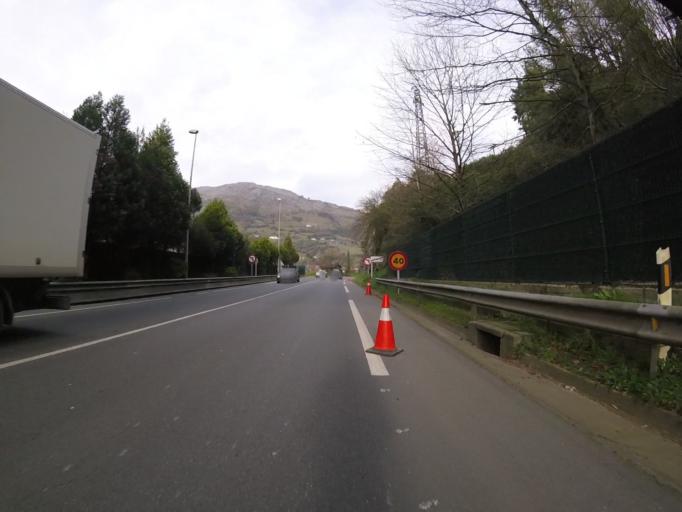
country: ES
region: Basque Country
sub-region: Provincia de Guipuzcoa
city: Azpeitia
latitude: 43.1819
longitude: -2.2602
